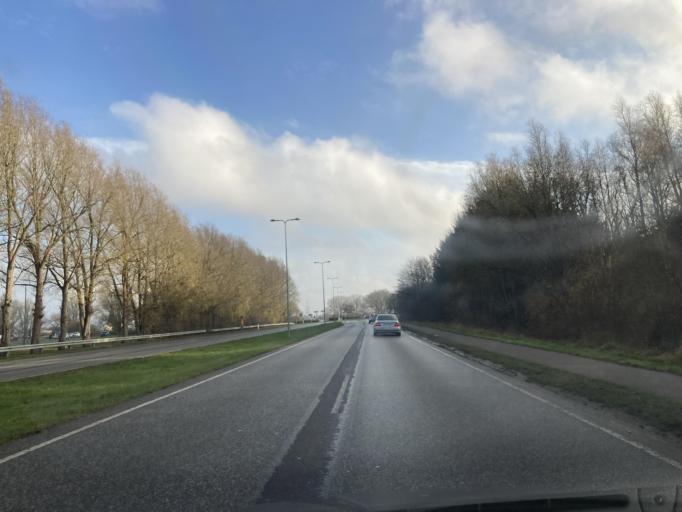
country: DK
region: Zealand
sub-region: Guldborgsund Kommune
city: Nykobing Falster
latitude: 54.7577
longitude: 11.8518
